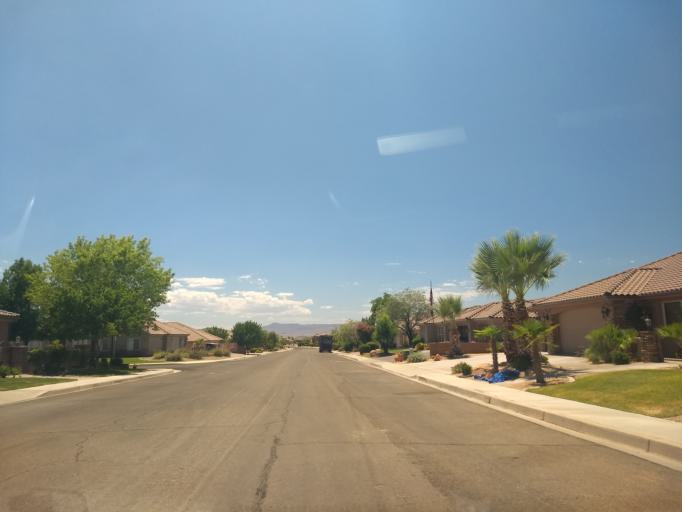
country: US
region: Utah
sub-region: Washington County
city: Washington
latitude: 37.1562
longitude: -113.5217
